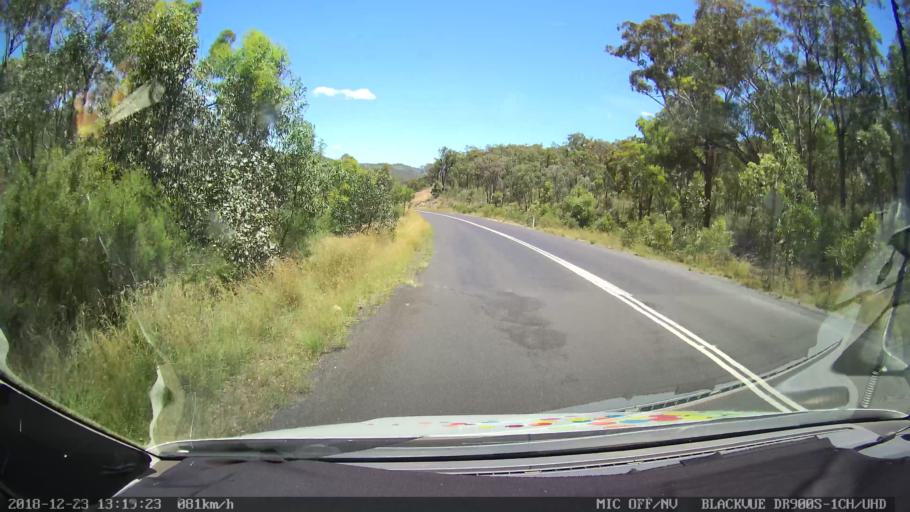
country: AU
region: New South Wales
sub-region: Armidale Dumaresq
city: Armidale
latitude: -30.4820
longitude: 151.4639
